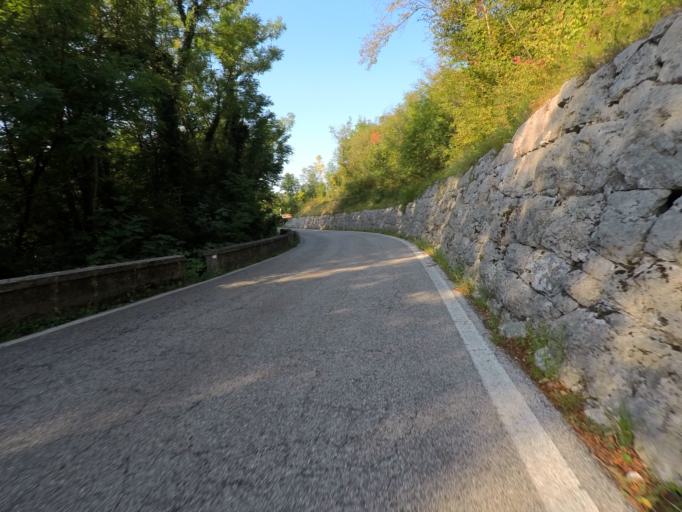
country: IT
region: Friuli Venezia Giulia
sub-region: Provincia di Udine
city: Forgaria nel Friuli
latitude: 46.2309
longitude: 13.0261
